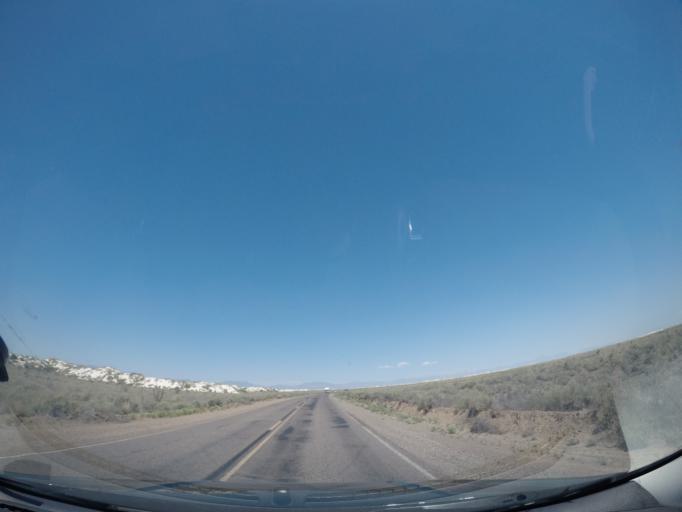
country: US
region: New Mexico
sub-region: Otero County
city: Holloman Air Force Base
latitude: 32.7882
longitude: -106.1898
